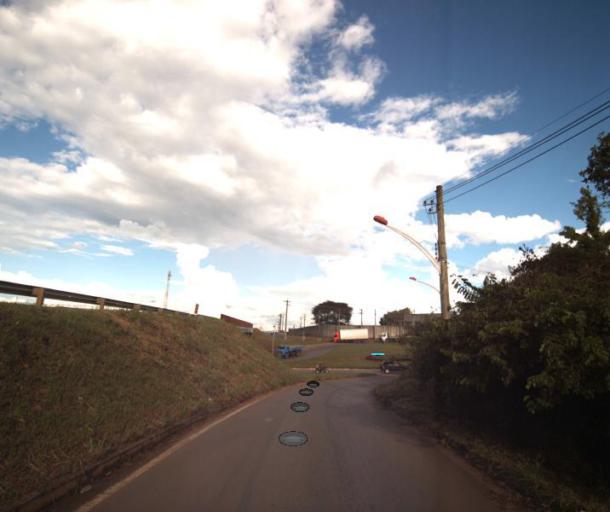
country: BR
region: Goias
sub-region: Anapolis
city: Anapolis
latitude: -16.2867
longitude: -48.9443
